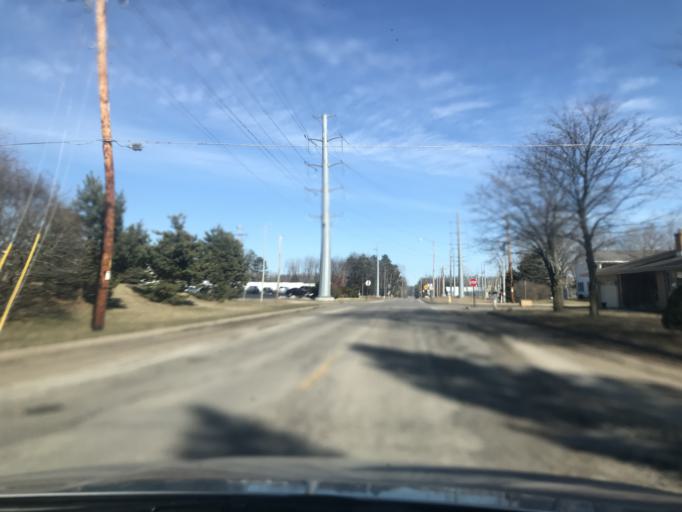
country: US
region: Michigan
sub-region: Menominee County
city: Menominee
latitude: 45.1443
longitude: -87.6182
